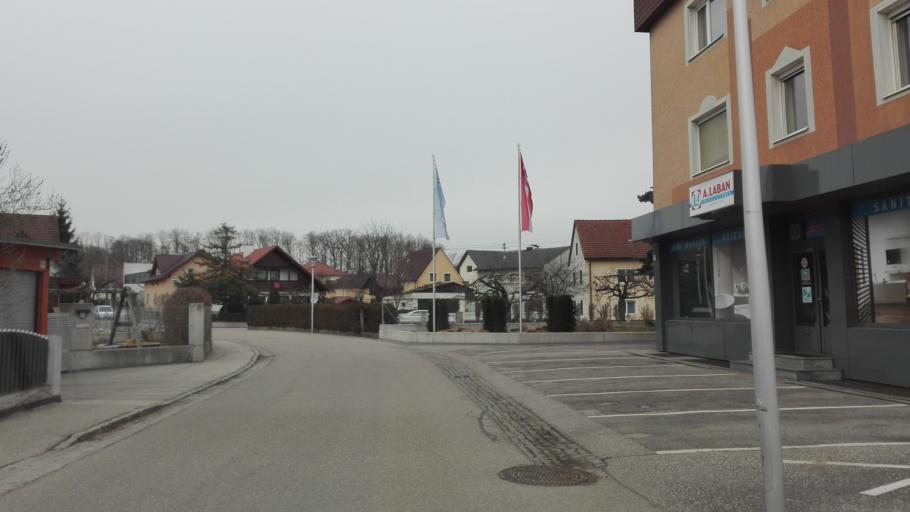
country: AT
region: Upper Austria
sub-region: Politischer Bezirk Linz-Land
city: Traun
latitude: 48.2464
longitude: 14.2428
